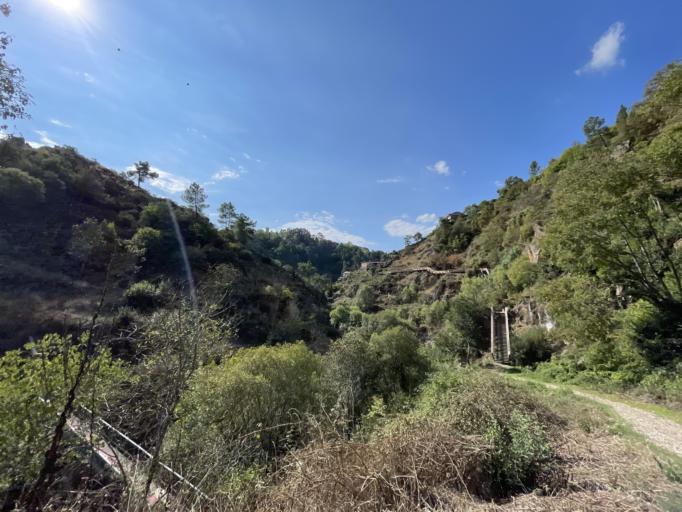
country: PT
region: Vila Real
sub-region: Vila Real
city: Vila Real
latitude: 41.2931
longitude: -7.7442
